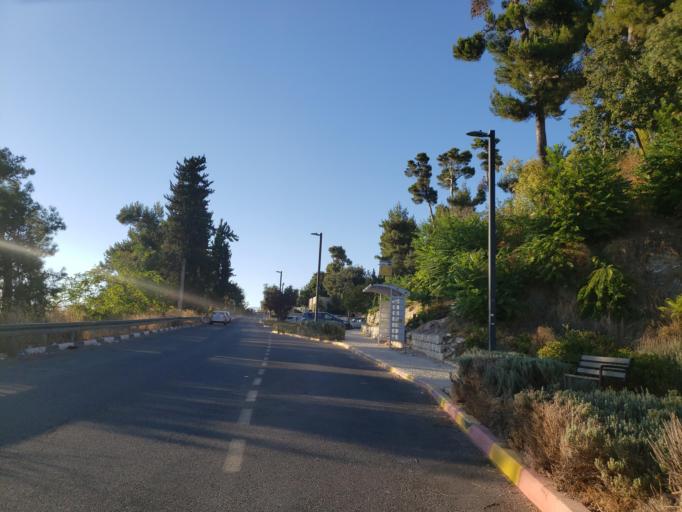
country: IL
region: Northern District
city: Safed
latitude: 32.9682
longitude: 35.4945
